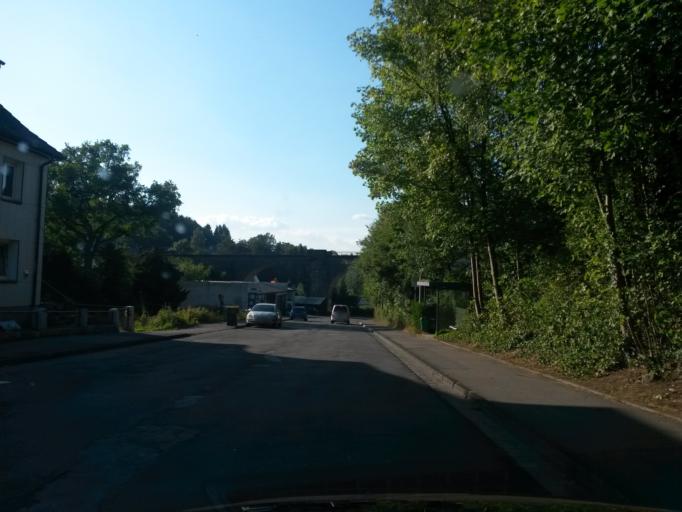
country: DE
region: North Rhine-Westphalia
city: Meinerzhagen
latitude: 51.1014
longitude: 7.6378
